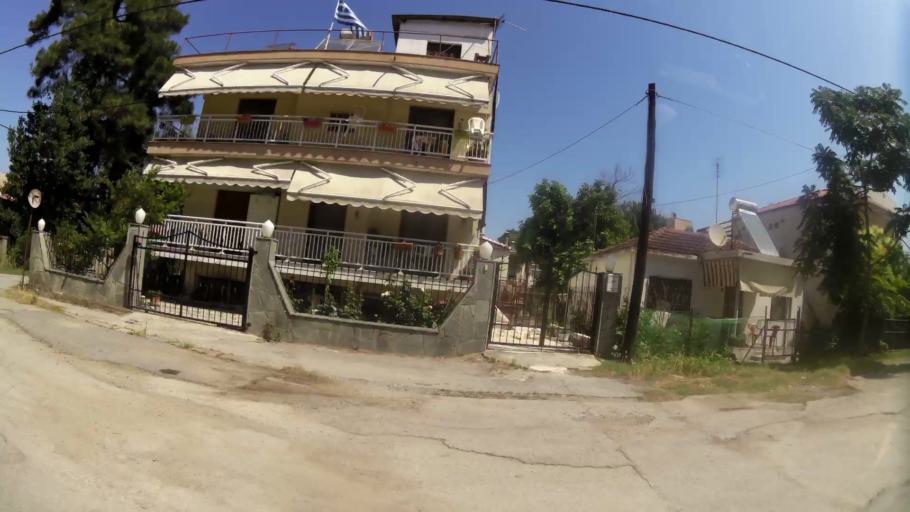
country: GR
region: Central Macedonia
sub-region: Nomos Thessalonikis
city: Agia Triada
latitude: 40.4990
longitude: 22.8737
